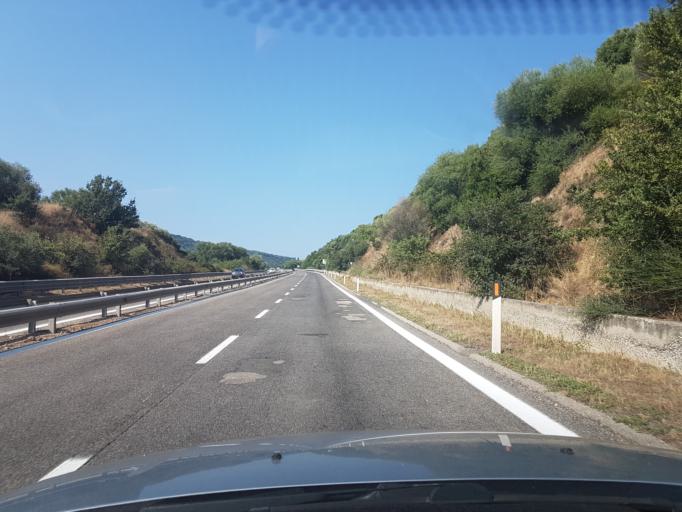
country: IT
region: Sardinia
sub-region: Provincia di Nuoro
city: Nuoro
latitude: 40.3426
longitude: 9.3136
